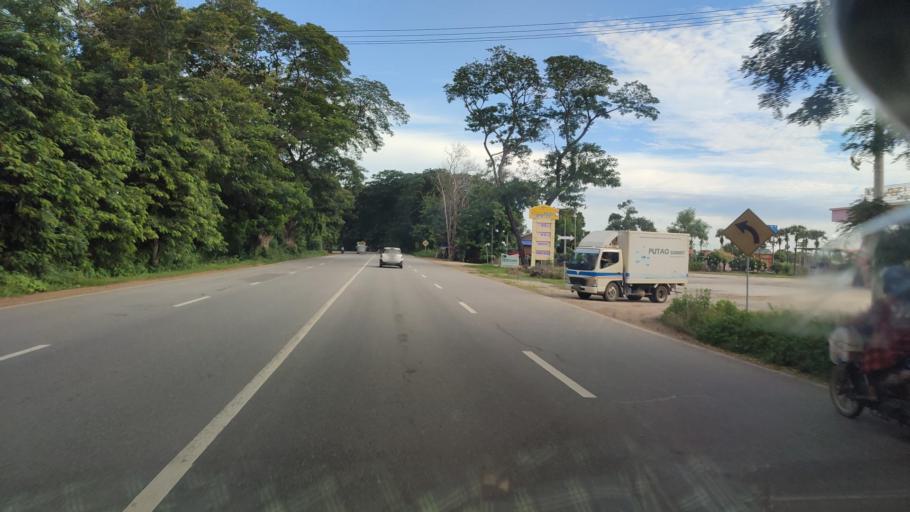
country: MM
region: Mandalay
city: Yamethin
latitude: 20.2218
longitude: 96.1803
